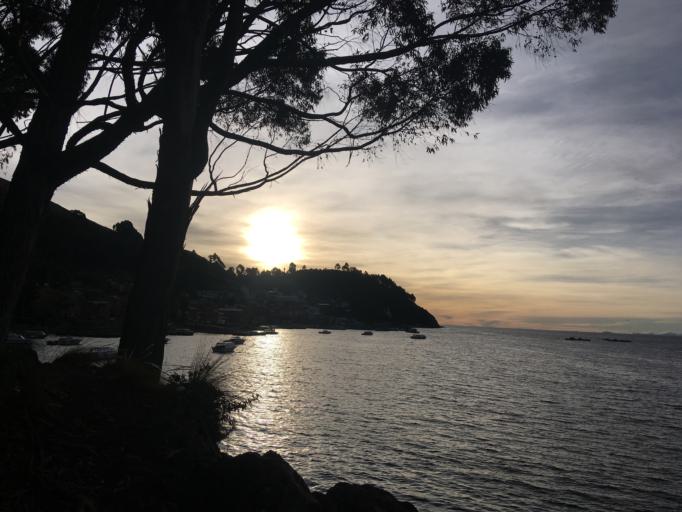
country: BO
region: La Paz
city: San Pedro
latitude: -16.2246
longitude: -68.8481
